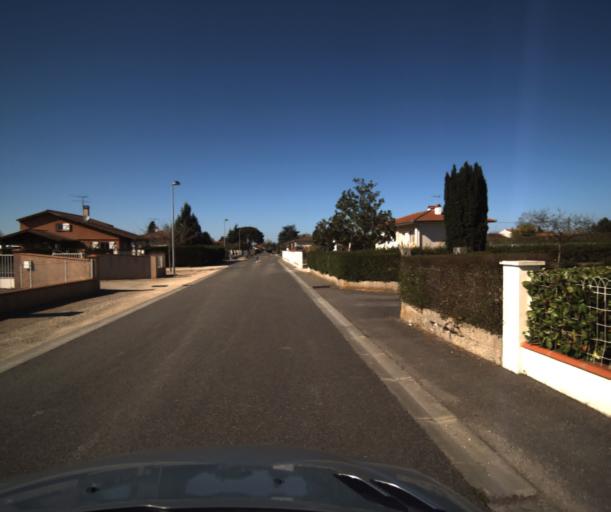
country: FR
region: Midi-Pyrenees
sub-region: Departement du Tarn-et-Garonne
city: Bressols
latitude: 43.9683
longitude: 1.3375
